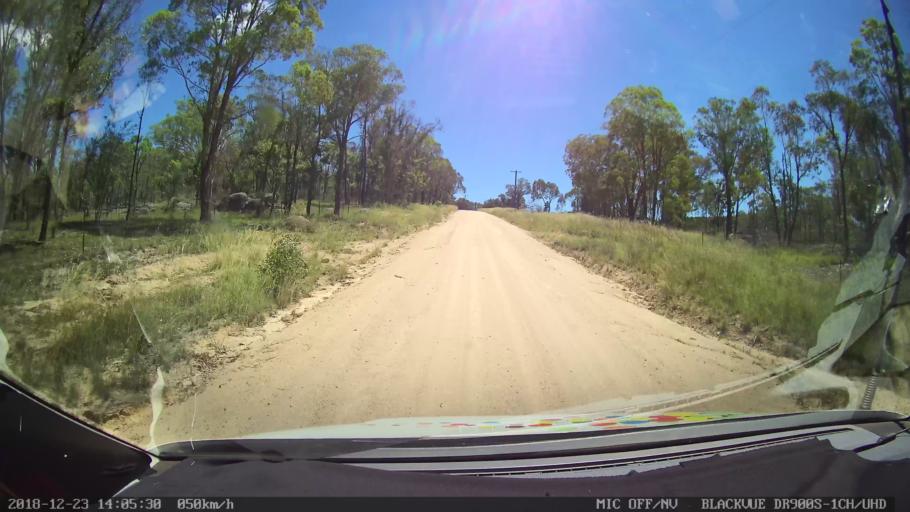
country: AU
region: New South Wales
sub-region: Tamworth Municipality
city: Manilla
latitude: -30.6250
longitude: 151.0803
